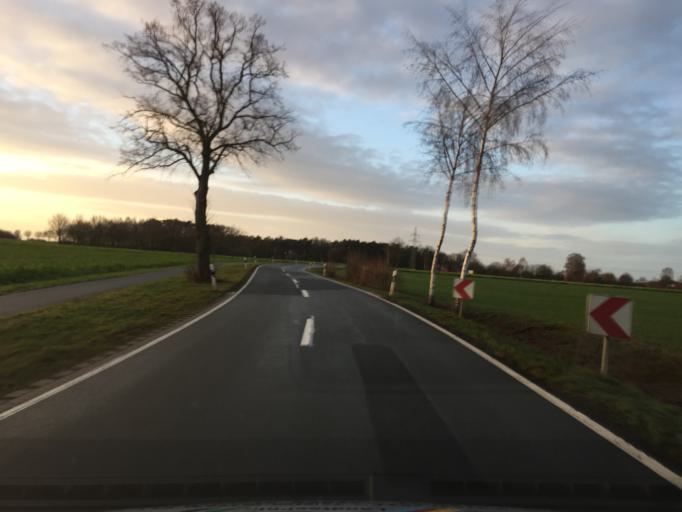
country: DE
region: Lower Saxony
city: Raddestorf
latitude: 52.4482
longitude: 8.9436
